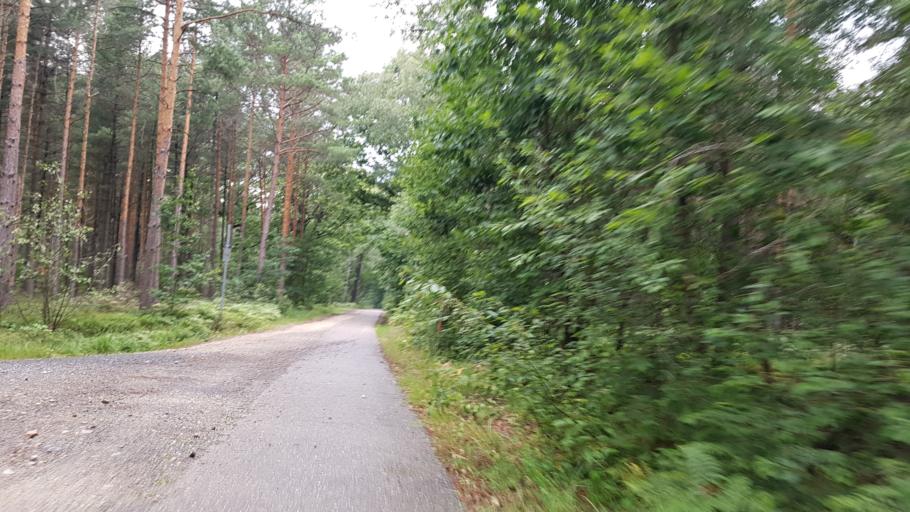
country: DE
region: Brandenburg
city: Schonborn
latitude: 51.6218
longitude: 13.4708
